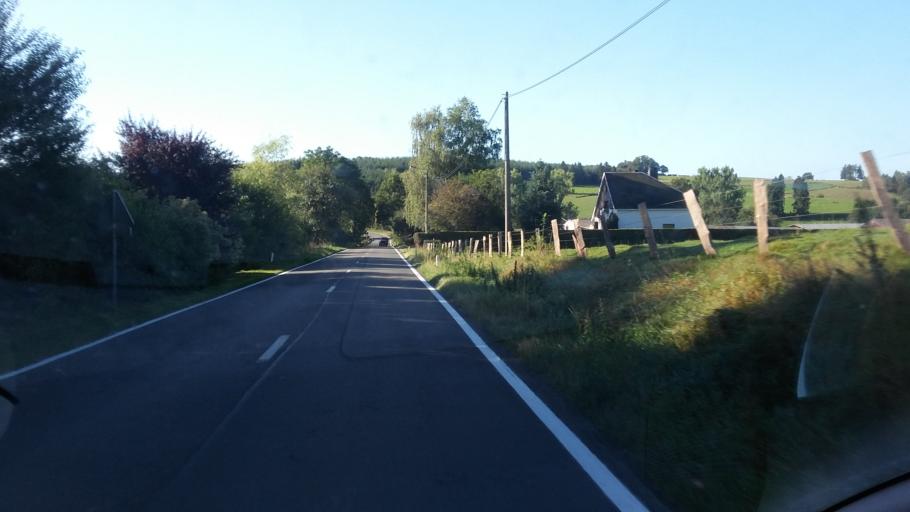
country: BE
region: Wallonia
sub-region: Province du Luxembourg
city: Neufchateau
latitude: 49.8344
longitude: 5.4160
